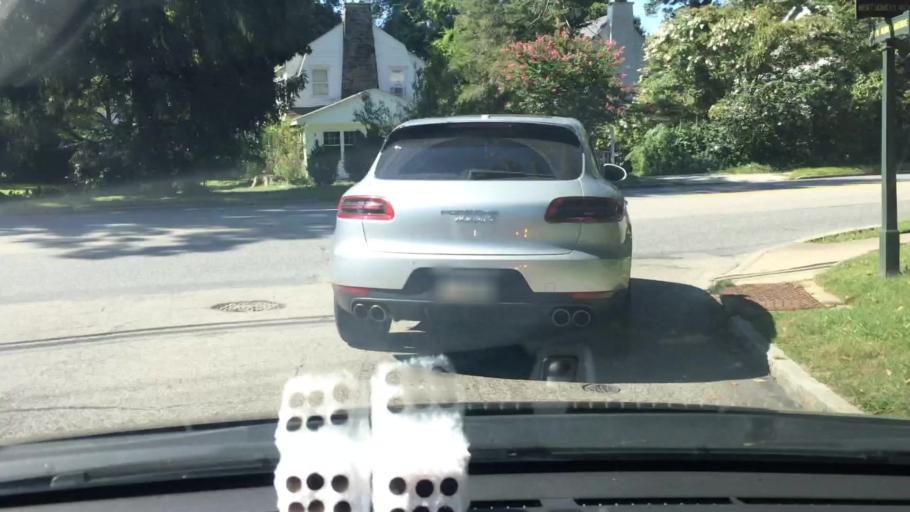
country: US
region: Pennsylvania
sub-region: Montgomery County
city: Narberth
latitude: 40.0135
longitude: -75.2657
